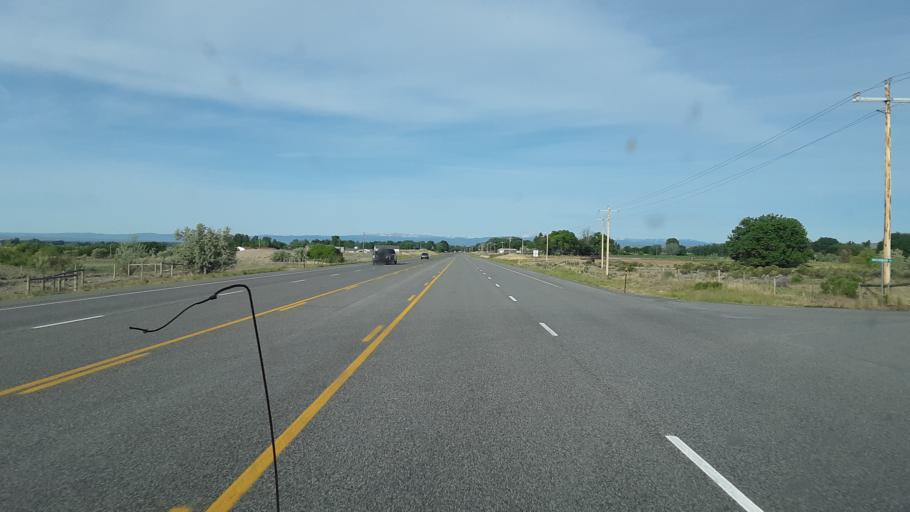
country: US
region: Wyoming
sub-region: Fremont County
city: Riverton
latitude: 43.1142
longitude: -108.3333
